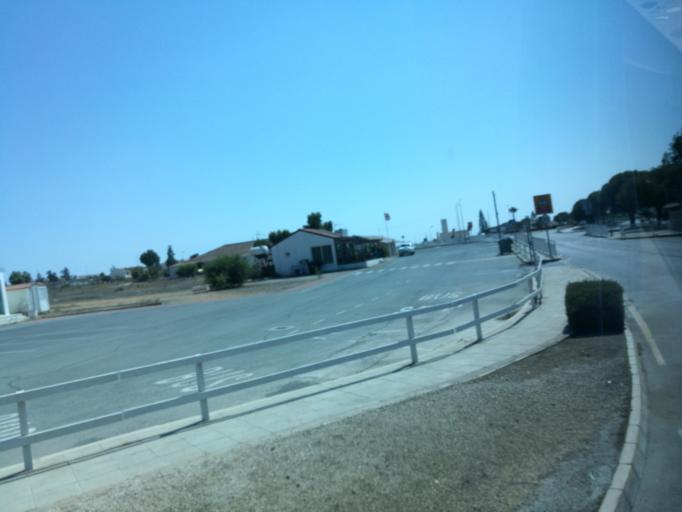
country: CY
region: Ammochostos
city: Acheritou
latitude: 35.0897
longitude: 33.8897
